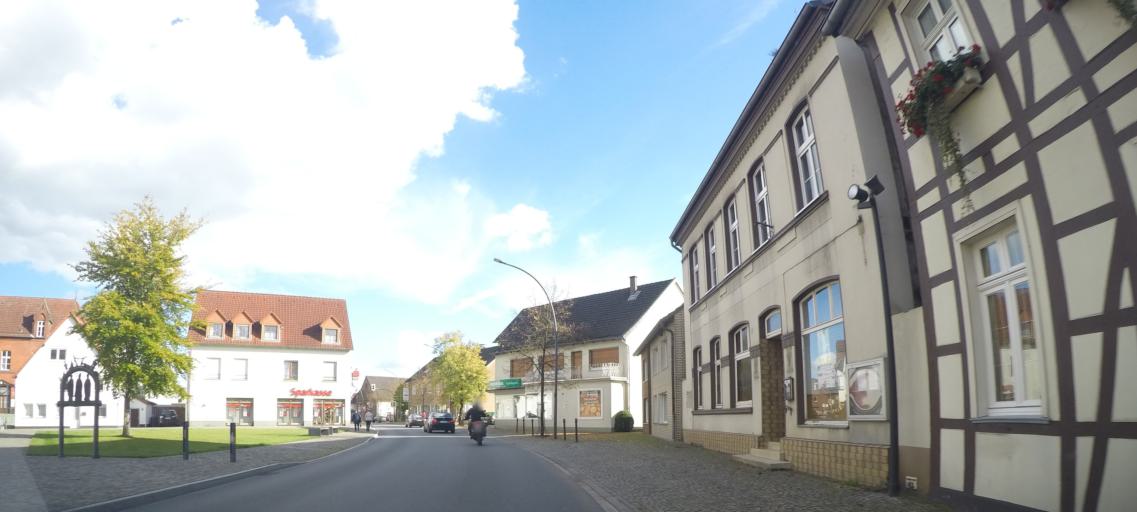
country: DE
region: North Rhine-Westphalia
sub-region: Regierungsbezirk Arnsberg
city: Welver
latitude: 51.6648
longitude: 8.0384
